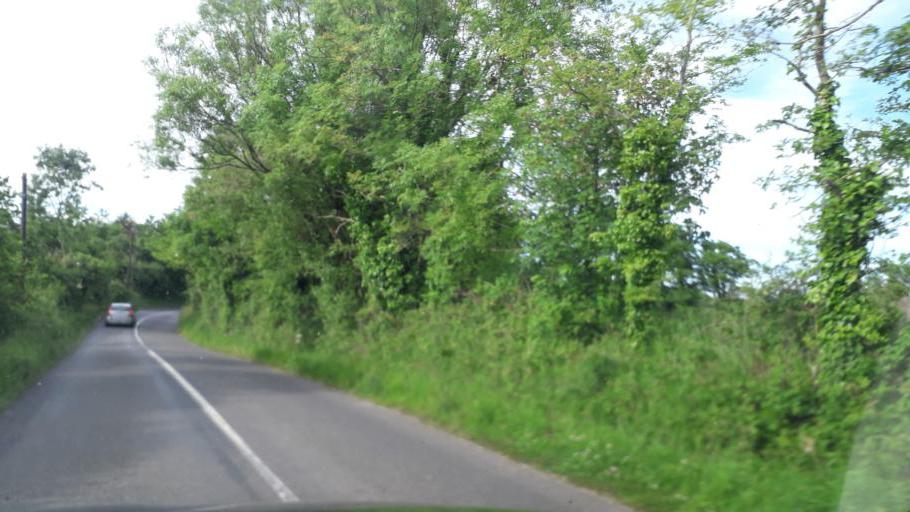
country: IE
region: Leinster
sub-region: Loch Garman
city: Courtown
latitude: 52.5621
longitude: -6.2322
